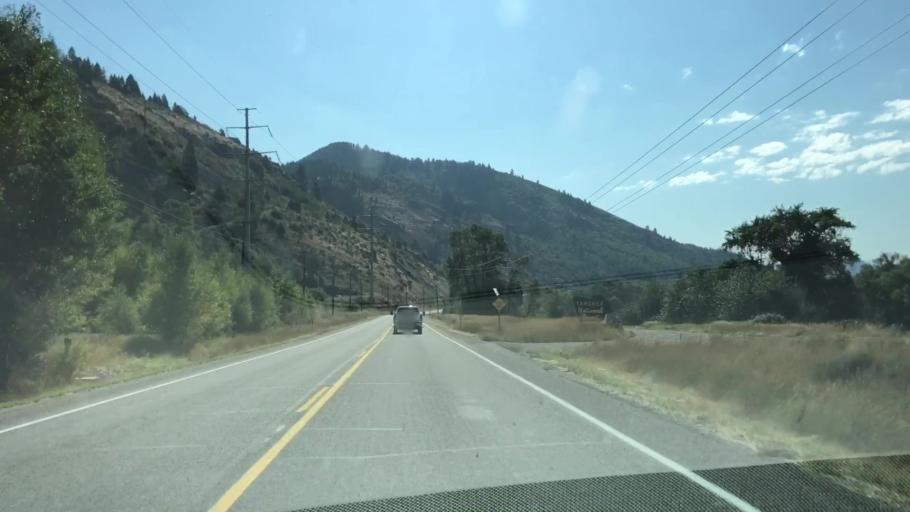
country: US
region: Idaho
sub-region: Teton County
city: Victor
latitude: 43.3480
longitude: -111.2124
